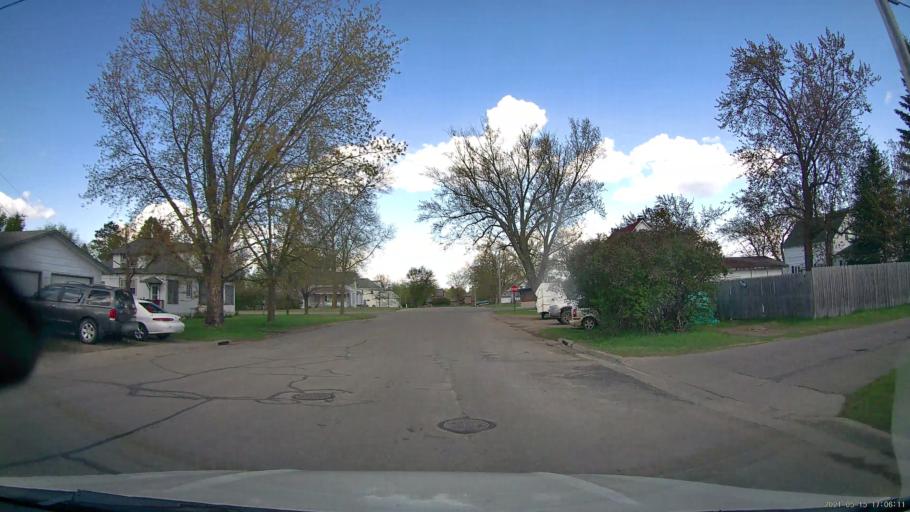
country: US
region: Minnesota
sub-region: Hubbard County
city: Park Rapids
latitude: 46.9235
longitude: -95.0611
